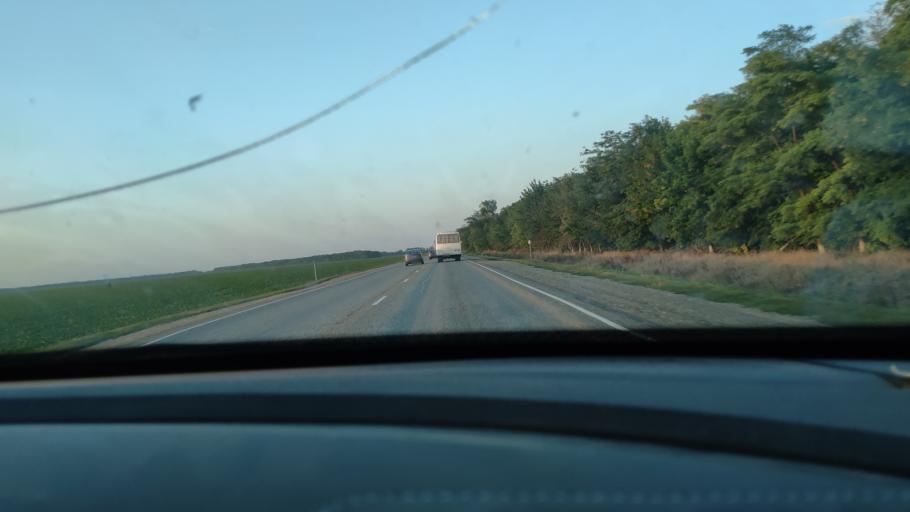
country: RU
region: Krasnodarskiy
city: Starominskaya
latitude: 46.4524
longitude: 39.0312
